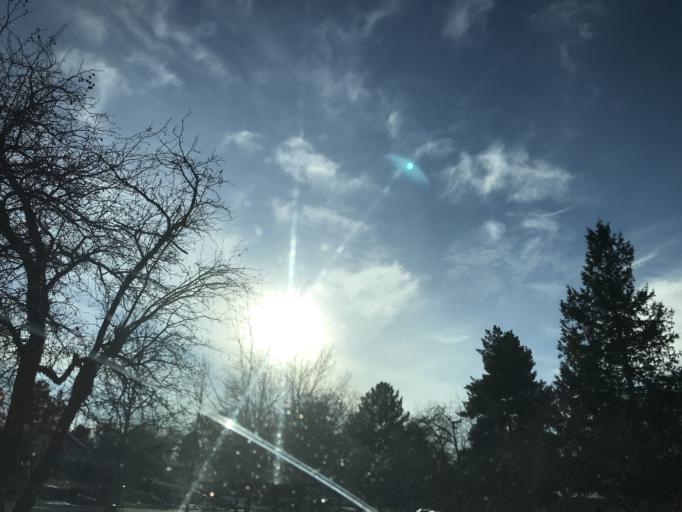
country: US
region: Colorado
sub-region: Arapahoe County
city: Littleton
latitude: 39.6067
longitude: -105.0105
